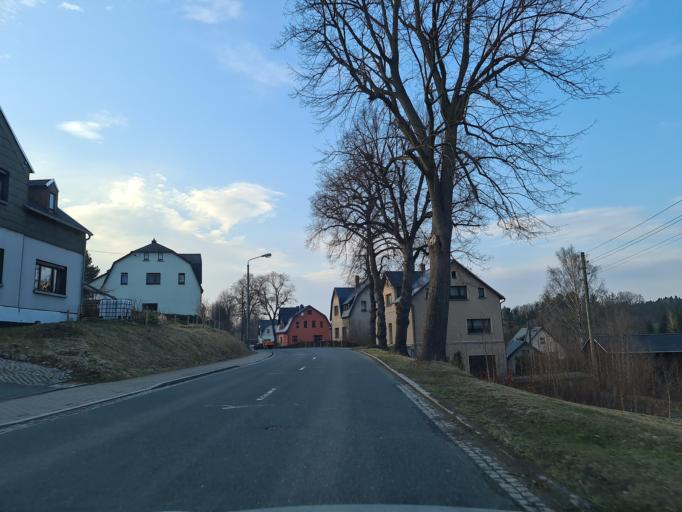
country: DE
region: Saxony
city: Auerbach
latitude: 50.5049
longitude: 12.4305
